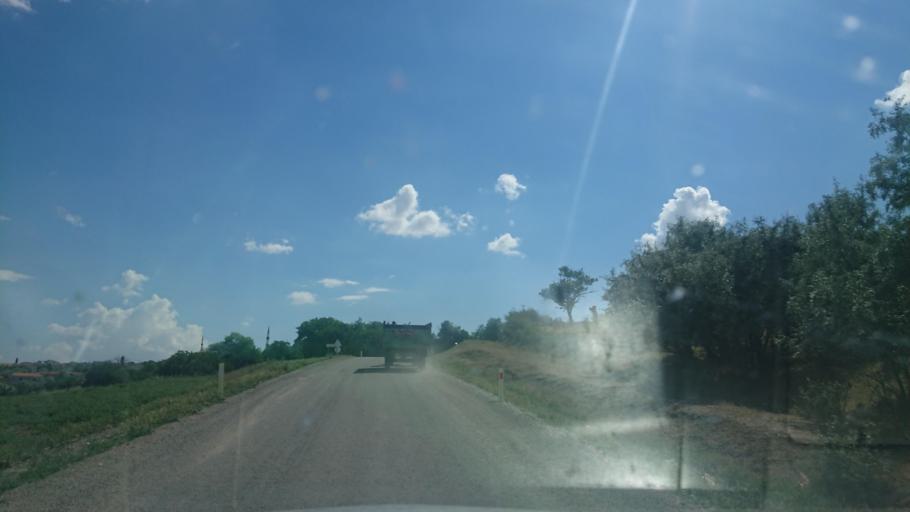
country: TR
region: Aksaray
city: Agacoren
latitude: 38.7757
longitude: 33.7884
